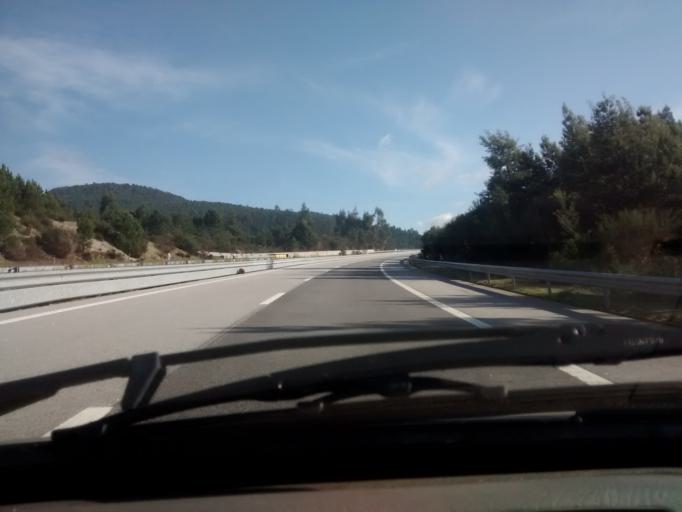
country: PT
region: Vila Real
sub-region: Mondim de Basto
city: Mondim de Basto
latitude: 41.4793
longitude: -7.8955
